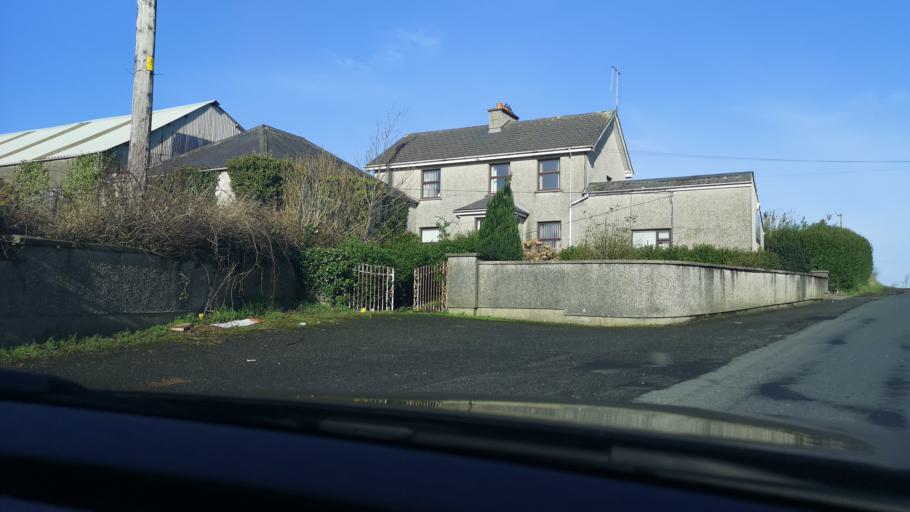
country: GB
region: Northern Ireland
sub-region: Newry and Mourne District
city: Newry
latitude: 54.1708
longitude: -6.3520
